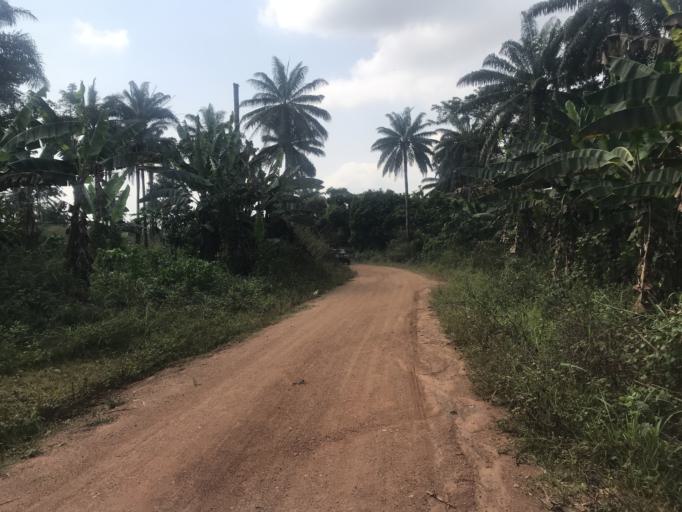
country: NG
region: Osun
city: Ikirun
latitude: 7.8551
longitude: 4.6301
